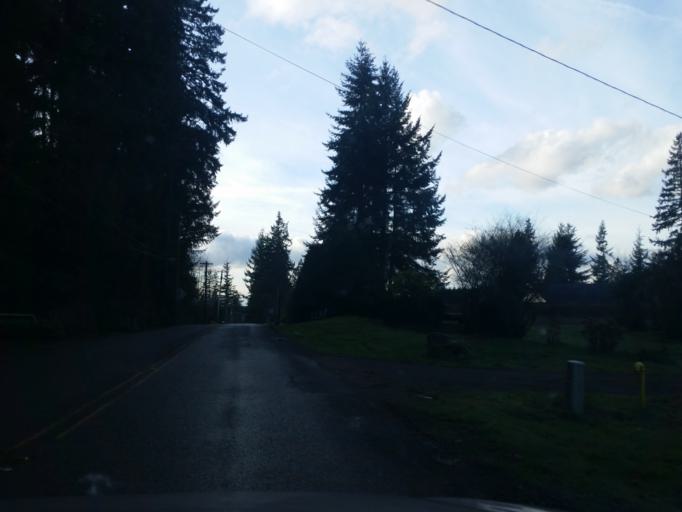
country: US
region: Washington
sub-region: Snohomish County
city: Maltby
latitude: 47.7795
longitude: -122.1325
